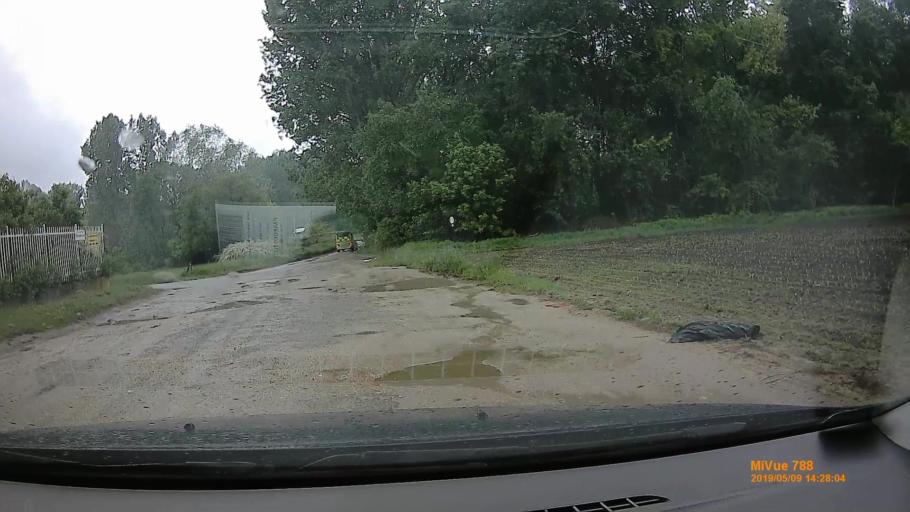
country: HU
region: Budapest
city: Budapest XVII. keruelet
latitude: 47.4911
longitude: 19.2209
